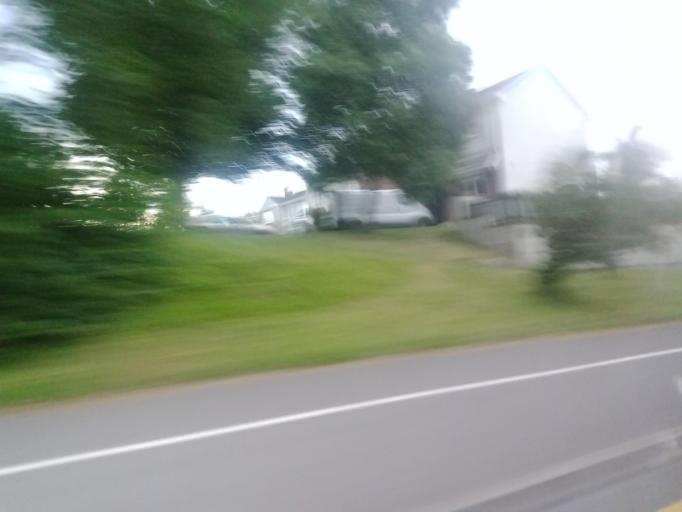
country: IE
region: Leinster
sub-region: Laois
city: Portlaoise
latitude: 53.0371
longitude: -7.3171
